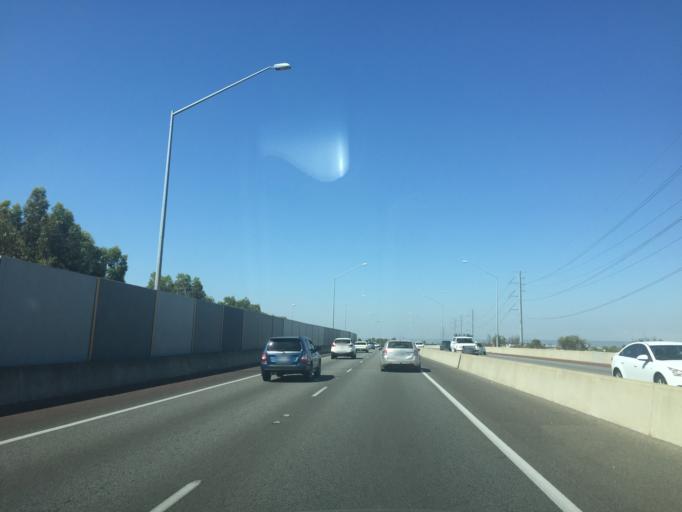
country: AU
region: Western Australia
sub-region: Canning
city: Willetton
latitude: -32.0706
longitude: 115.8885
